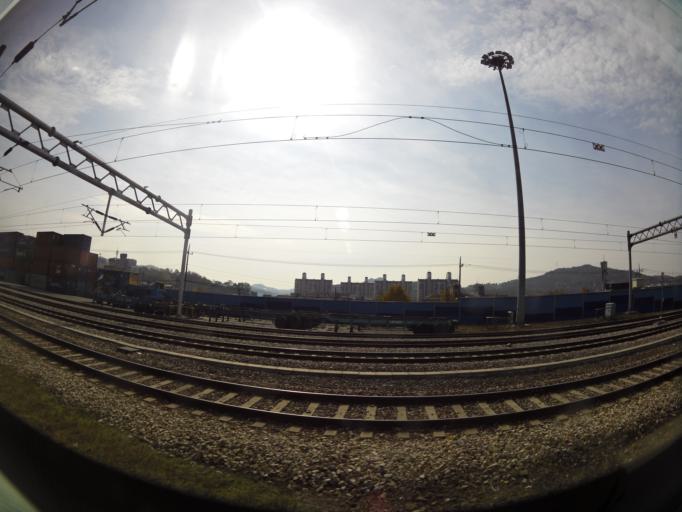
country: KR
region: Daejeon
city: Songgang-dong
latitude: 36.5331
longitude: 127.3622
